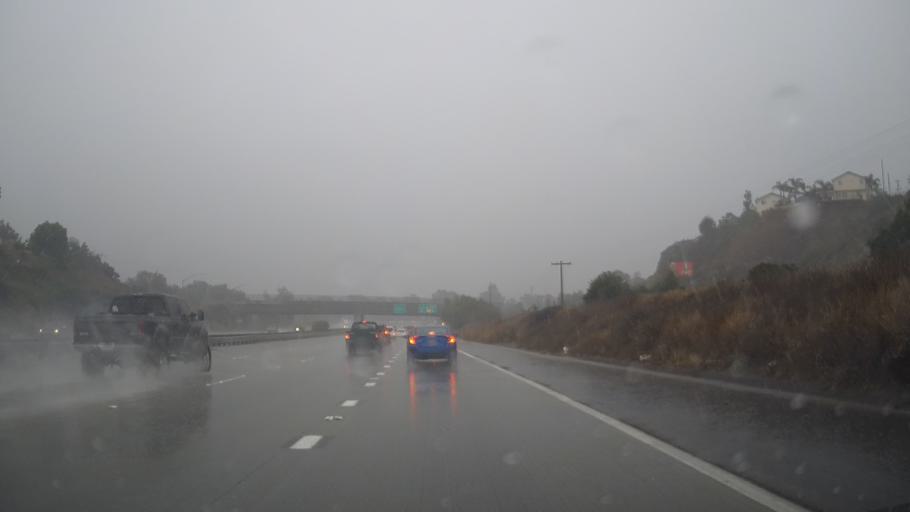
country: US
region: California
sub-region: San Diego County
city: Chula Vista
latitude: 32.6620
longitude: -117.0662
